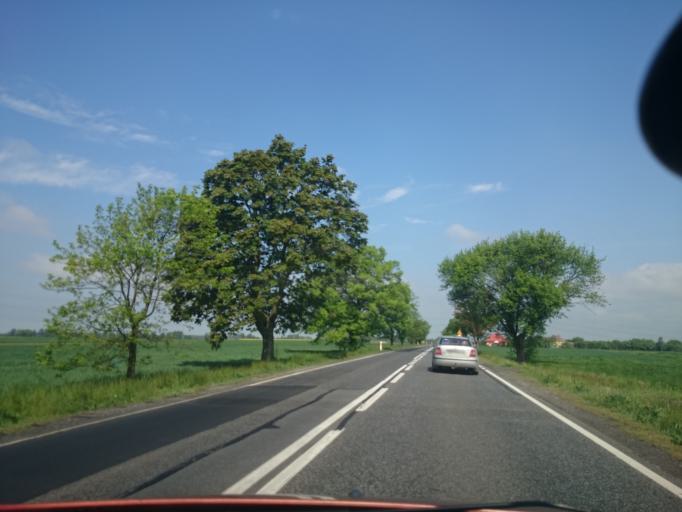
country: PL
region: Opole Voivodeship
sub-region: Powiat opolski
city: Dabrowa
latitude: 50.7111
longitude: 17.7763
